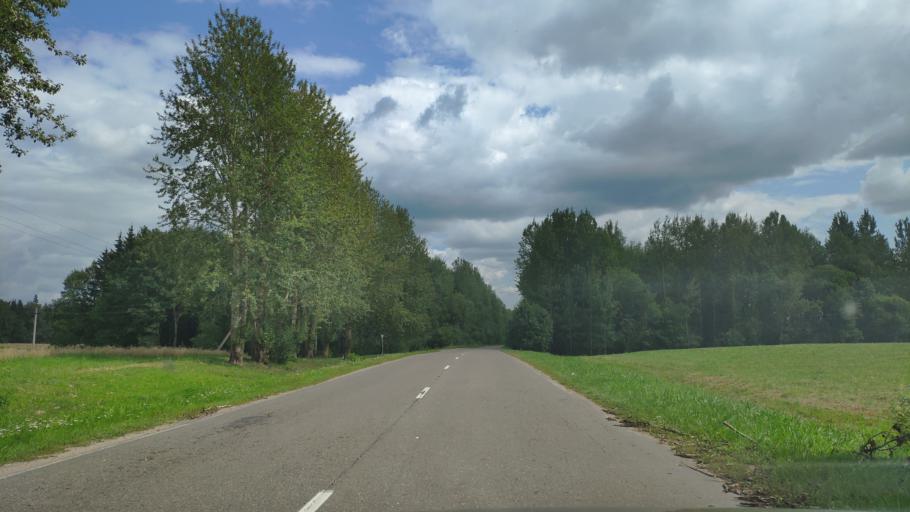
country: BY
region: Minsk
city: Khatsyezhyna
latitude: 53.8783
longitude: 27.2872
